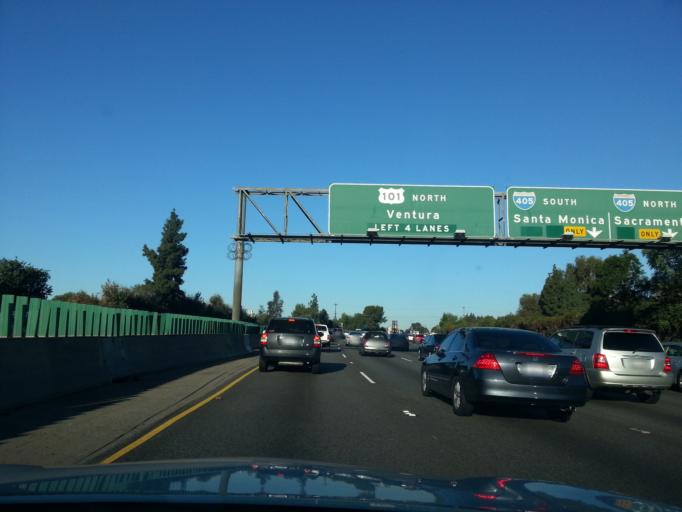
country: US
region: California
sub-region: Los Angeles County
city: Sherman Oaks
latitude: 34.1579
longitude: -118.4540
